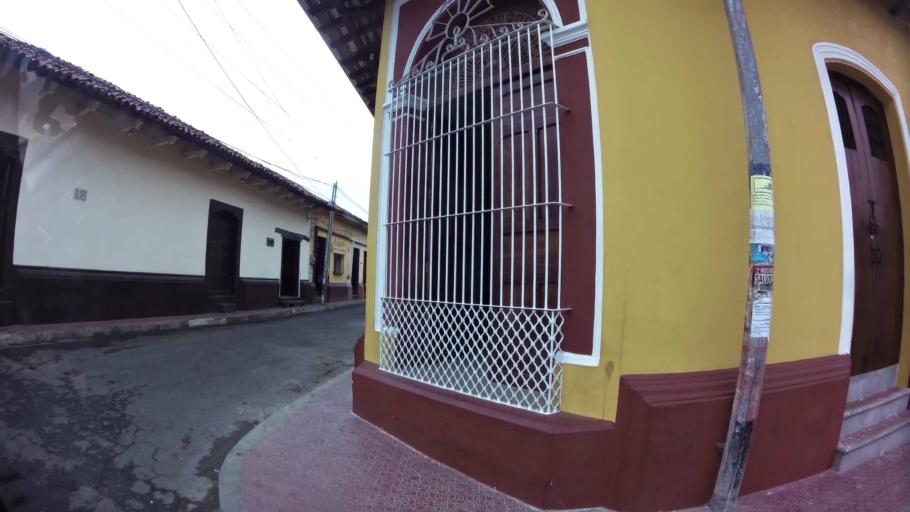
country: NI
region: Leon
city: Leon
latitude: 12.4350
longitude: -86.8830
